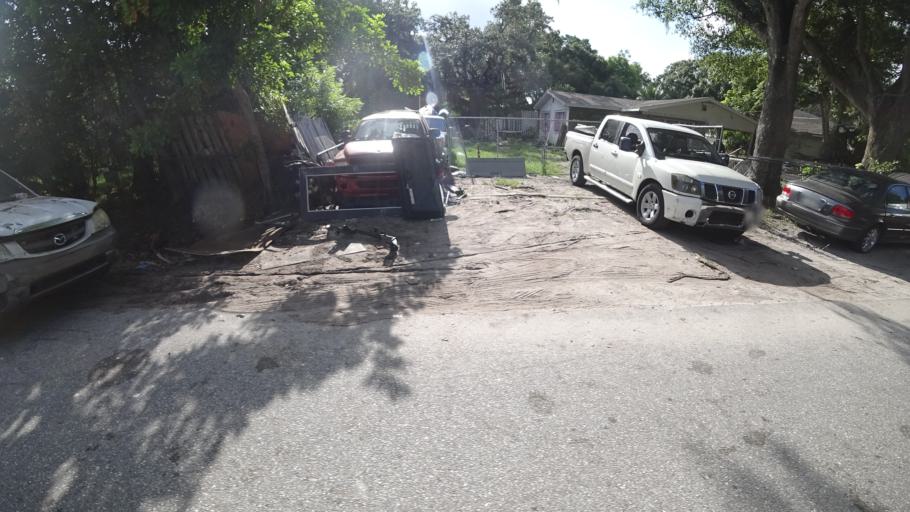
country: US
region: Florida
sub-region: Manatee County
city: Whitfield
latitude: 27.4386
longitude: -82.5569
